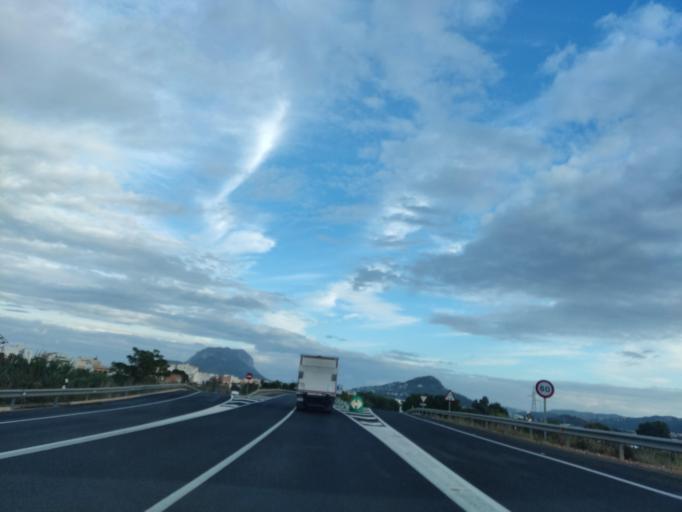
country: ES
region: Valencia
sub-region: Provincia de Alicante
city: Ondara
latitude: 38.8260
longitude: 0.0101
